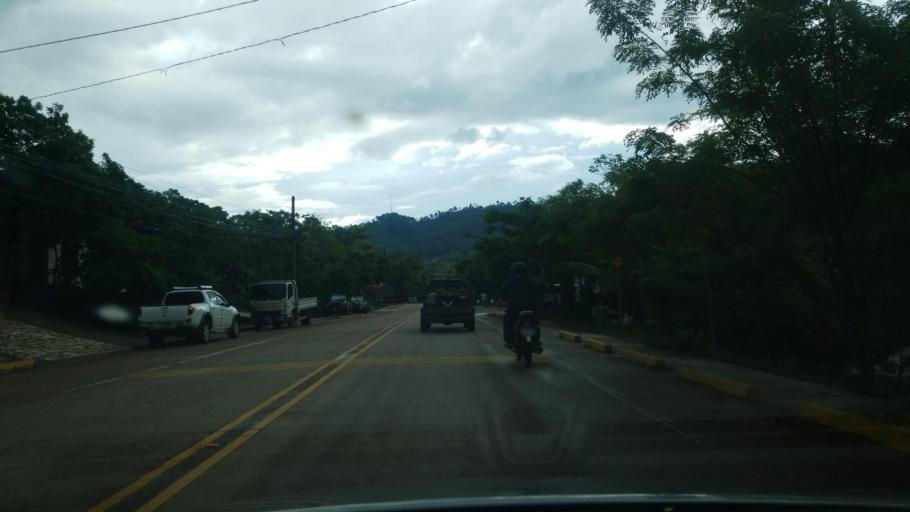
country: HN
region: Copan
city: Copan
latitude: 14.8421
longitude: -89.1675
